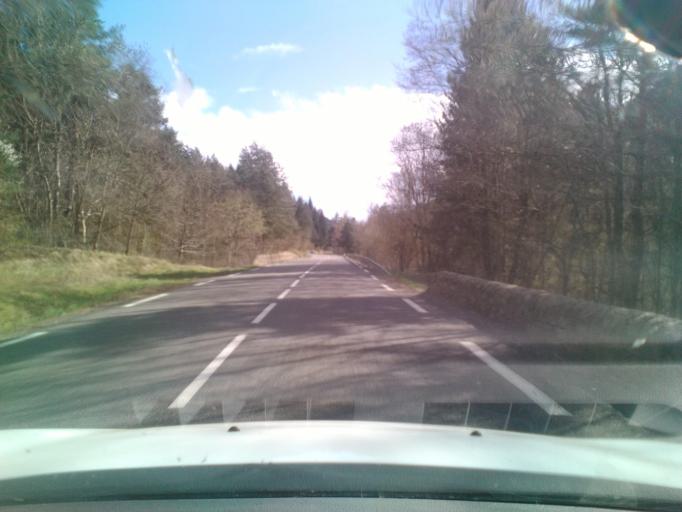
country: FR
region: Languedoc-Roussillon
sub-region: Departement de la Lozere
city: Mende
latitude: 44.4431
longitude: 3.5568
